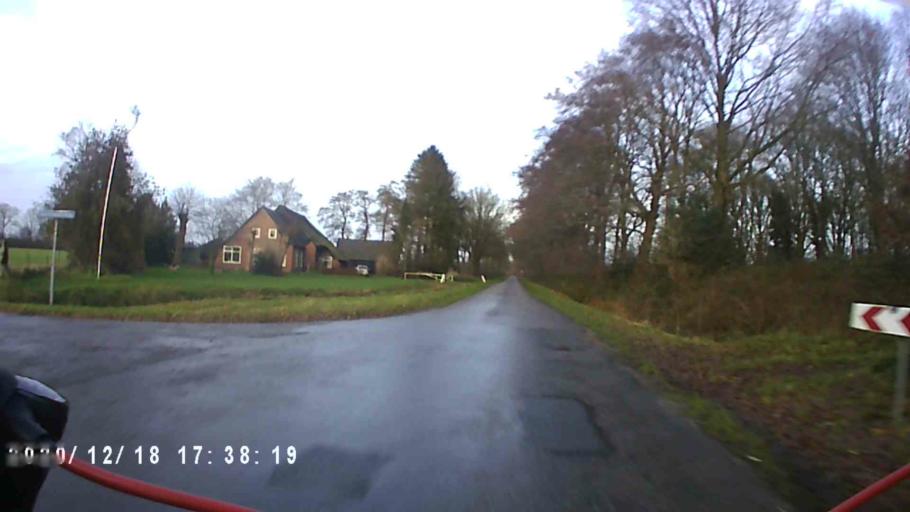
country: NL
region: Drenthe
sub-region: Gemeente Tynaarlo
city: Vries
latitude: 53.0872
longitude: 6.5774
